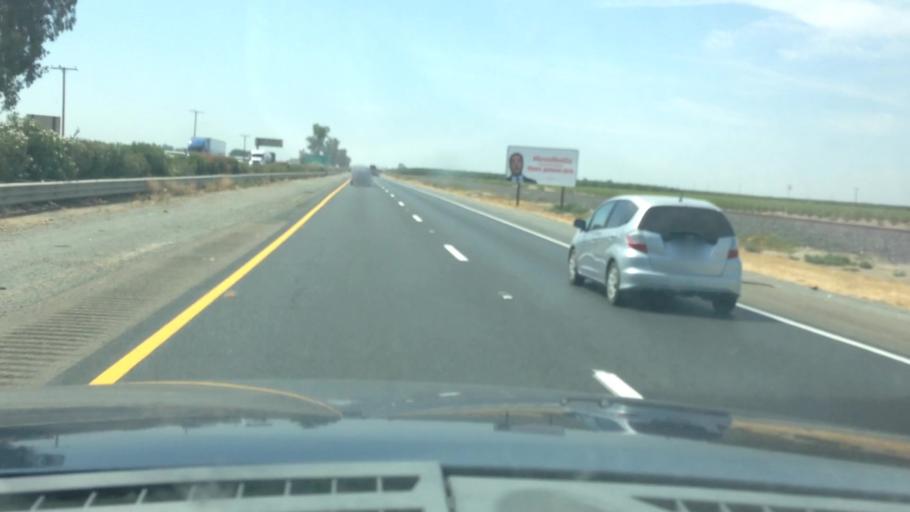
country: US
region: California
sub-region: Tulare County
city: Tipton
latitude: 36.0446
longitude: -119.3111
